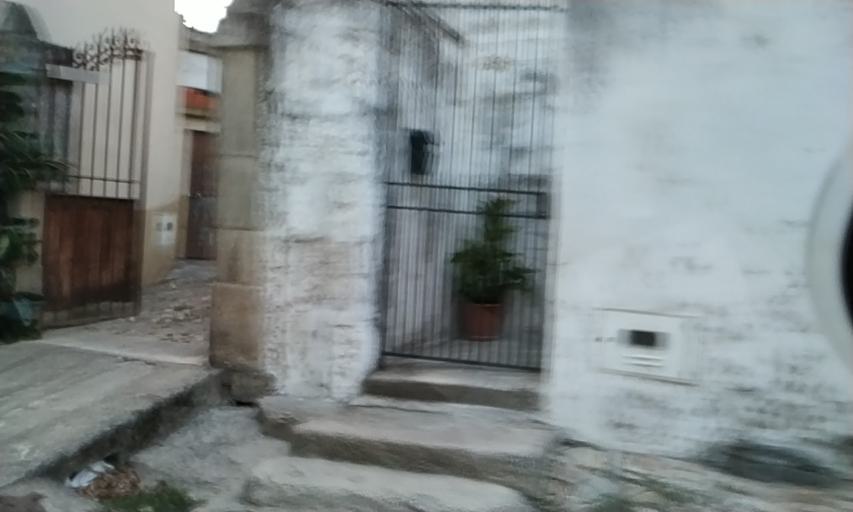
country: PT
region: Vila Real
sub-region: Peso da Regua
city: Peso da Regua
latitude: 41.1612
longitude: -7.7863
